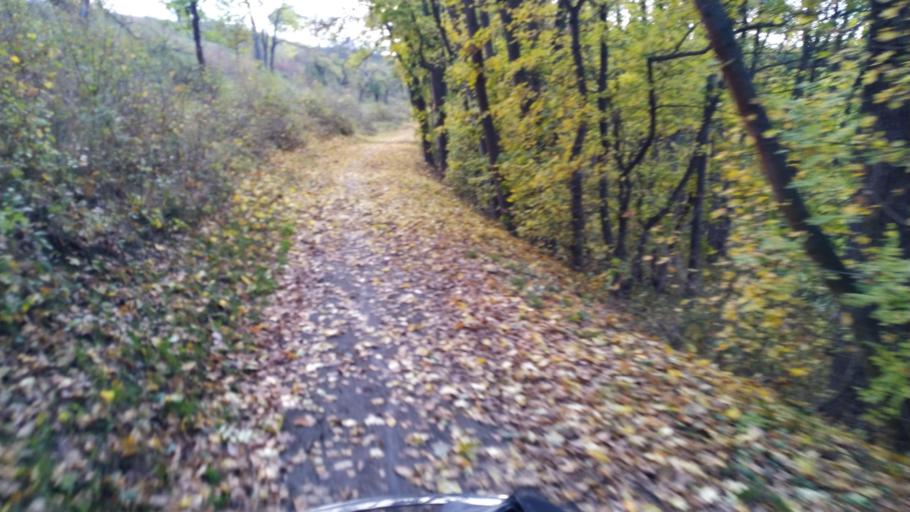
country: DE
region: Thuringia
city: Mattstedt
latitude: 51.0580
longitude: 11.5263
